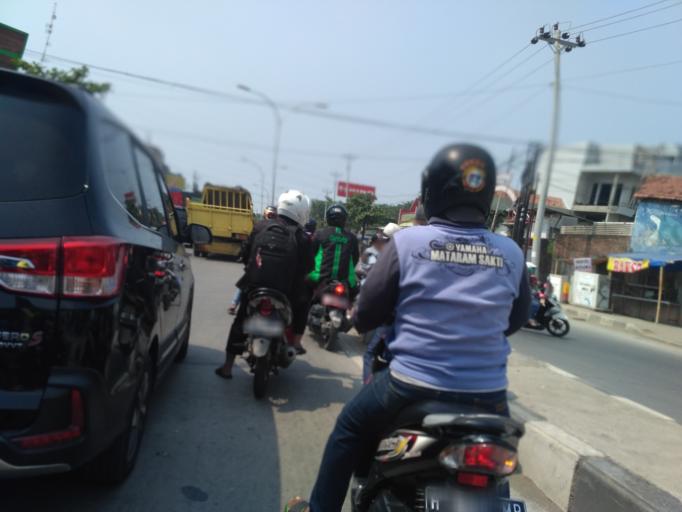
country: ID
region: Central Java
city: Semarang
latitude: -6.9591
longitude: 110.4445
